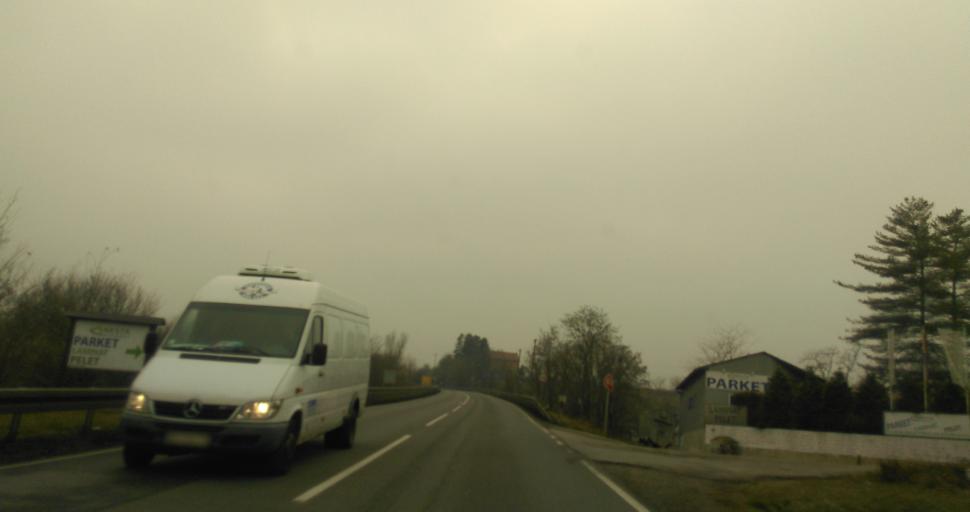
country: RS
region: Central Serbia
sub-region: Belgrade
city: Zvezdara
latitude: 44.7181
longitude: 20.5085
